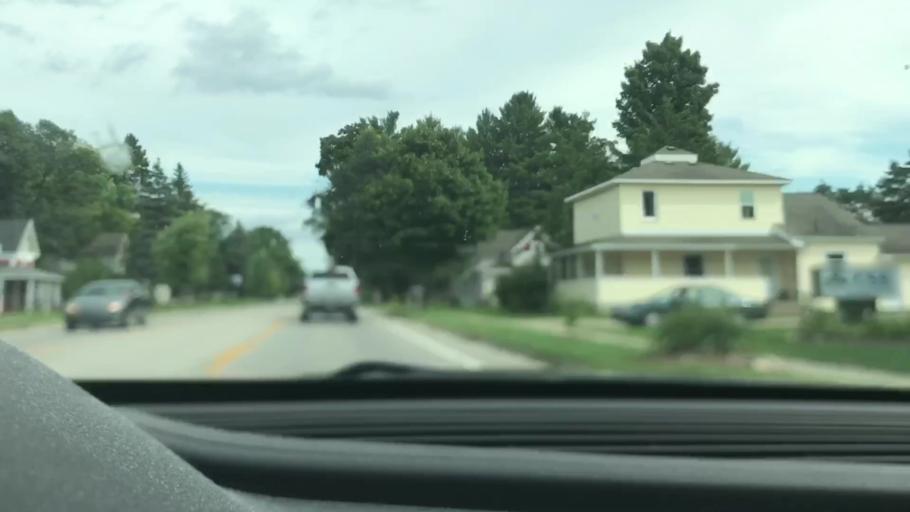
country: US
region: Michigan
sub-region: Antrim County
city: Bellaire
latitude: 44.9754
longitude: -85.2033
